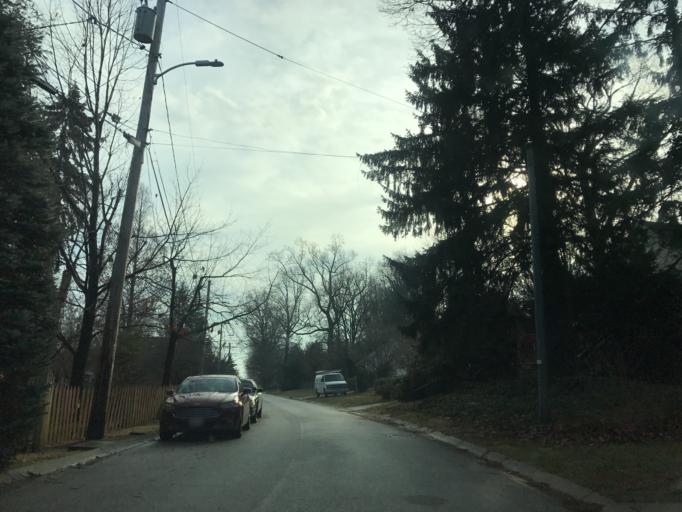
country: US
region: Maryland
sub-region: Baltimore County
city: Overlea
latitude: 39.3518
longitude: -76.5392
